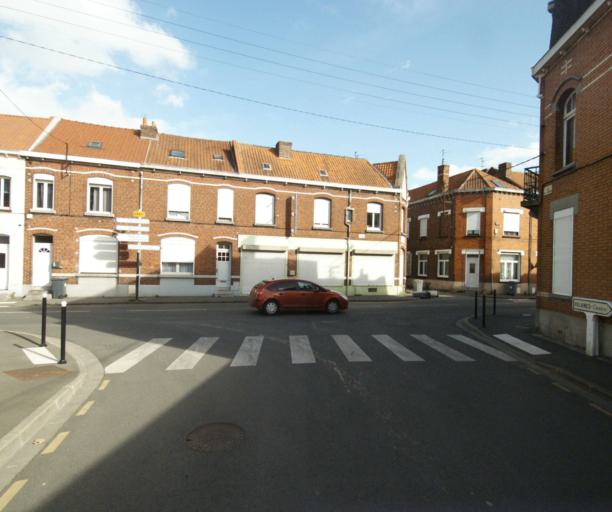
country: FR
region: Nord-Pas-de-Calais
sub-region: Departement du Nord
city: La Bassee
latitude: 50.5346
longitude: 2.8017
